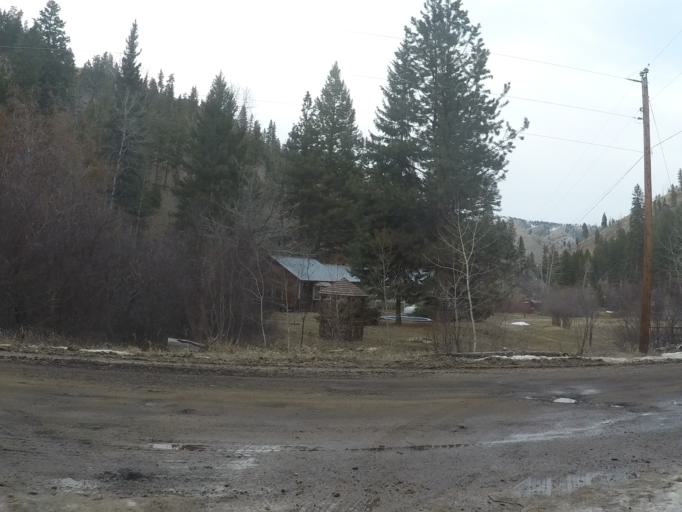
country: US
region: Montana
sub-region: Ravalli County
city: Hamilton
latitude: 45.8439
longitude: -114.0380
